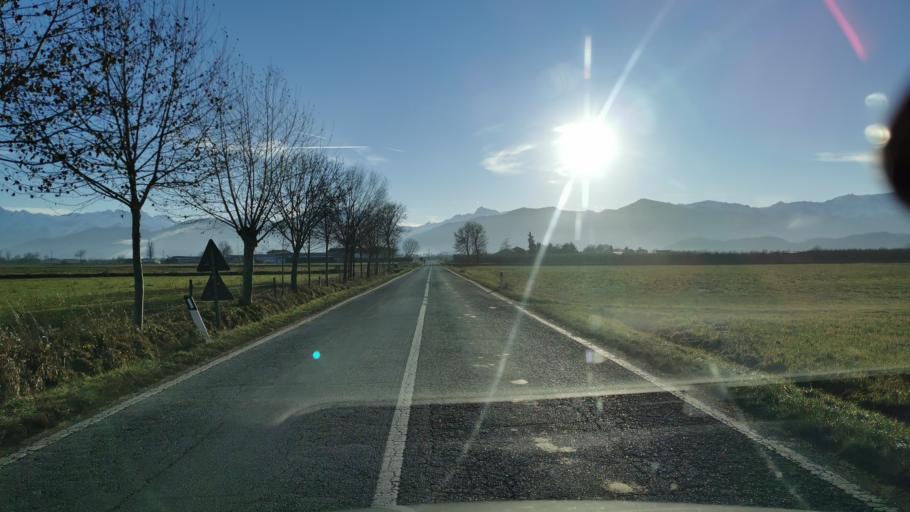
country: IT
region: Piedmont
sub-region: Provincia di Cuneo
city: Caraglio
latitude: 44.4437
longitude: 7.4693
